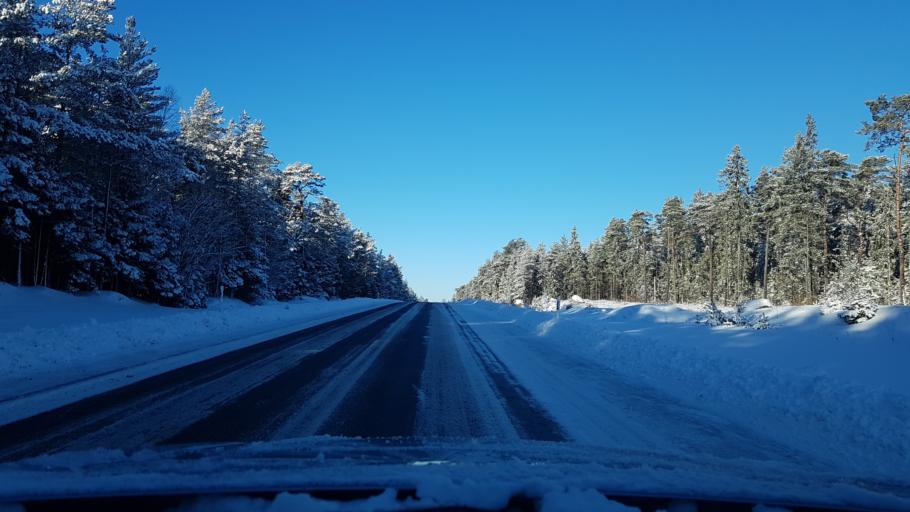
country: EE
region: Hiiumaa
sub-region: Kaerdla linn
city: Kardla
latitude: 58.9591
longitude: 22.8554
